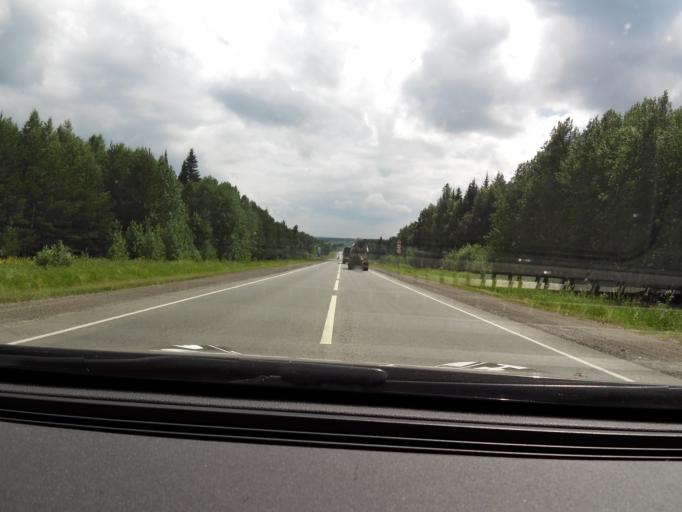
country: RU
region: Perm
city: Kungur
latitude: 57.3131
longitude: 56.9728
